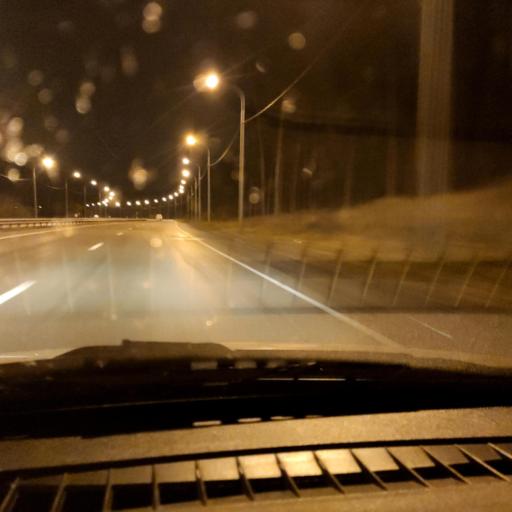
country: RU
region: Samara
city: Zhigulevsk
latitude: 53.5374
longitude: 49.5166
